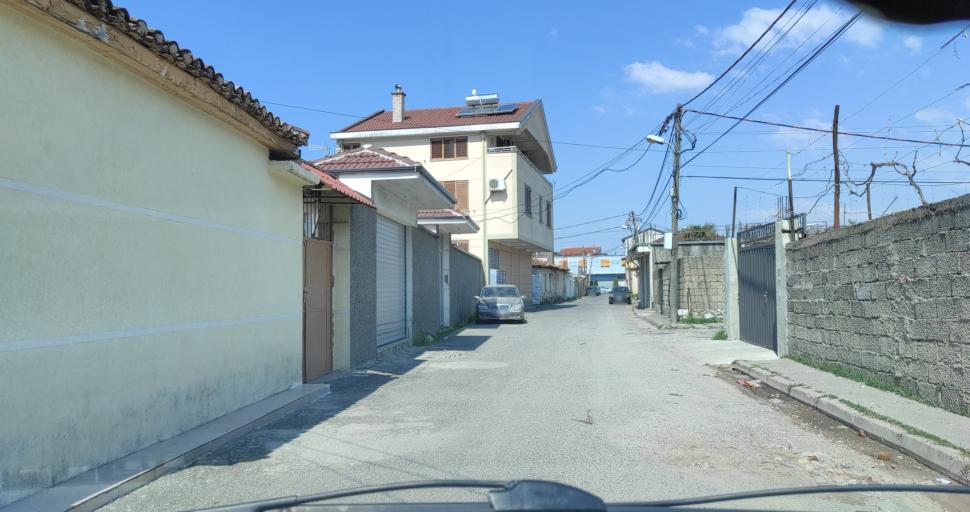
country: AL
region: Shkoder
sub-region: Rrethi i Shkodres
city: Shkoder
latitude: 42.0726
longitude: 19.5116
